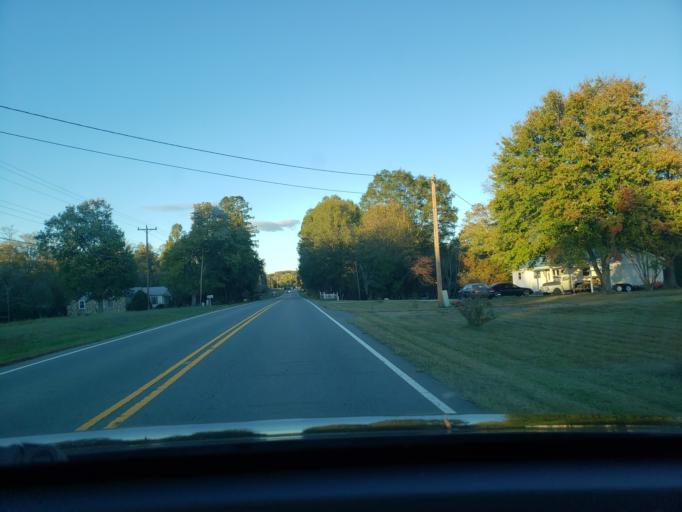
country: US
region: North Carolina
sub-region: Stokes County
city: Danbury
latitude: 36.3350
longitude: -80.2229
